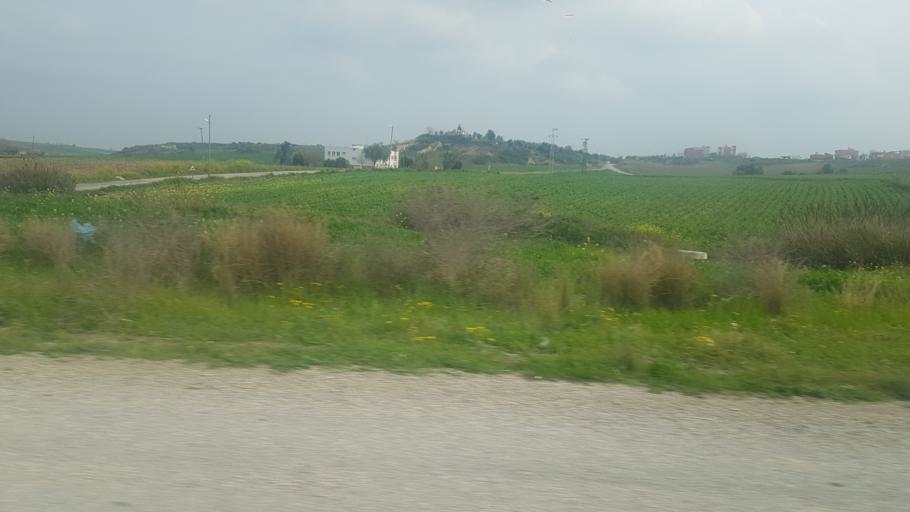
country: TR
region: Adana
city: Seyhan
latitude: 37.0489
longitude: 35.2007
